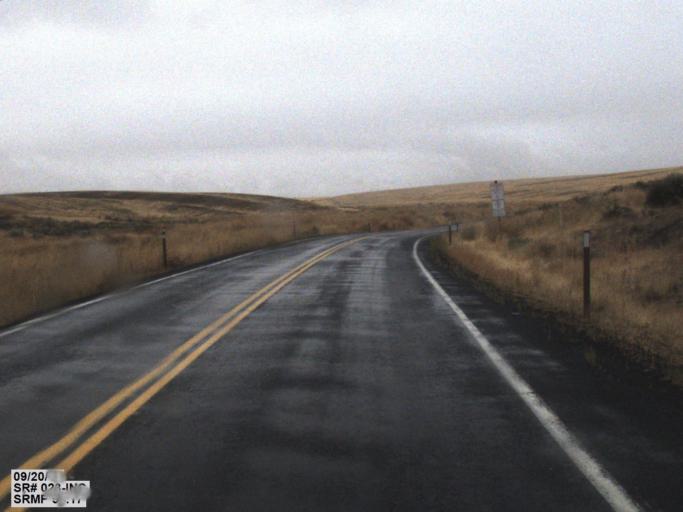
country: US
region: Washington
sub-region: Lincoln County
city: Davenport
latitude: 47.3770
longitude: -118.1221
